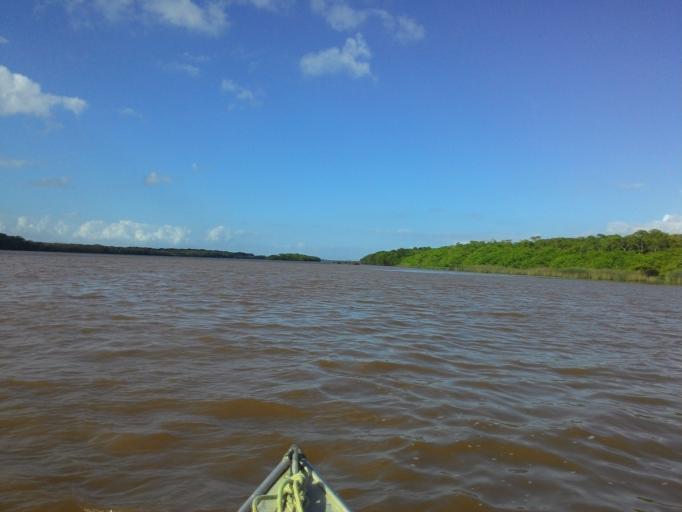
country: BR
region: Sao Paulo
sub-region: Pariquera-Acu
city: Pariquera Acu
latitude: -24.8415
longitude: -47.7419
